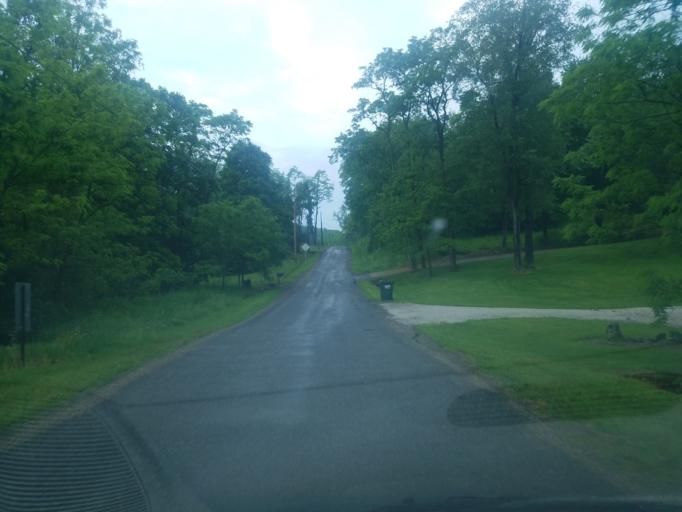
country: US
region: Ohio
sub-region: Stark County
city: Minerva
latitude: 40.7772
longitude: -80.9556
